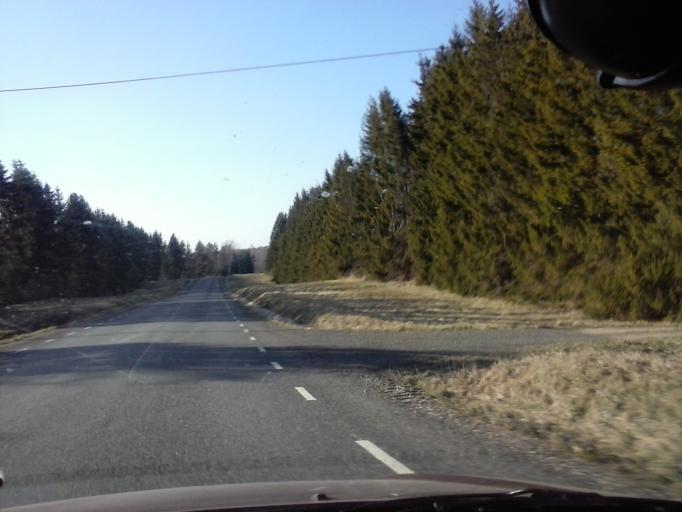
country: EE
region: Tartu
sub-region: UElenurme vald
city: Ulenurme
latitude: 58.1692
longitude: 26.8377
